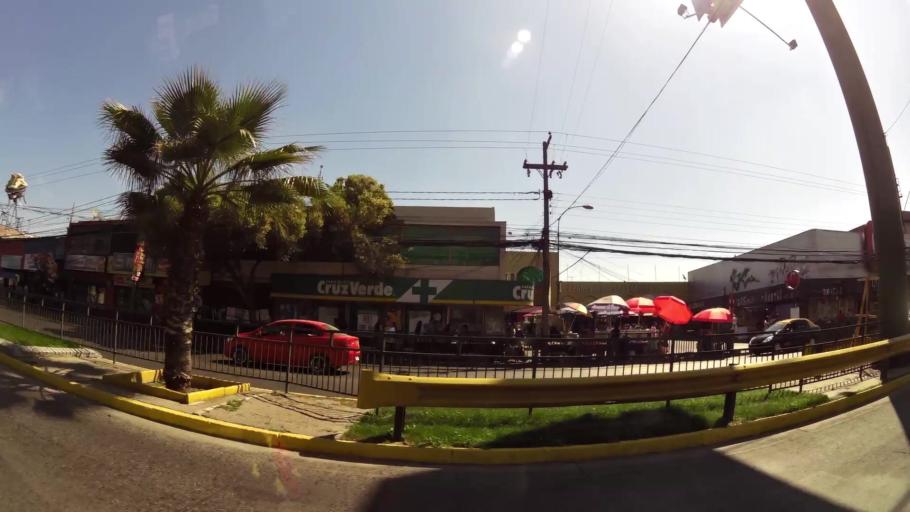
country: CL
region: Santiago Metropolitan
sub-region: Provincia de Santiago
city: Santiago
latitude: -33.5174
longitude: -70.6588
